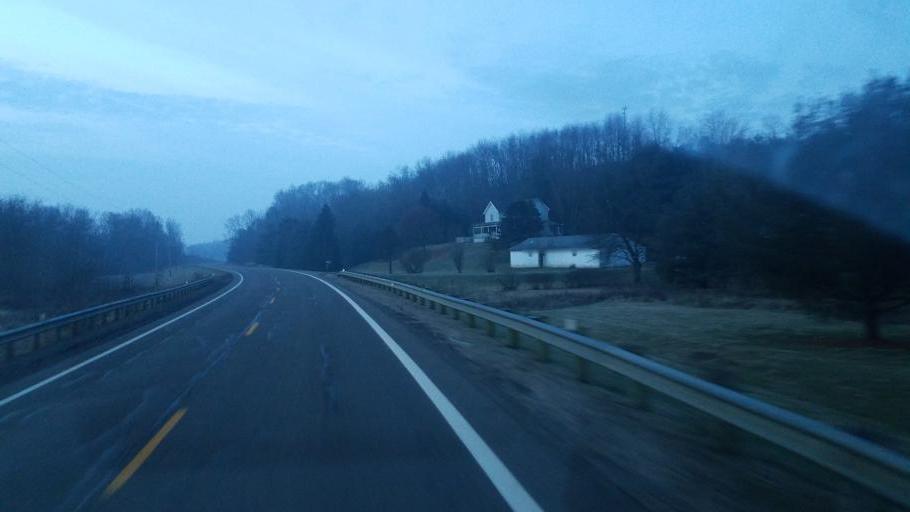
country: US
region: Ohio
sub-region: Coshocton County
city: West Lafayette
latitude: 40.3167
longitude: -81.7487
